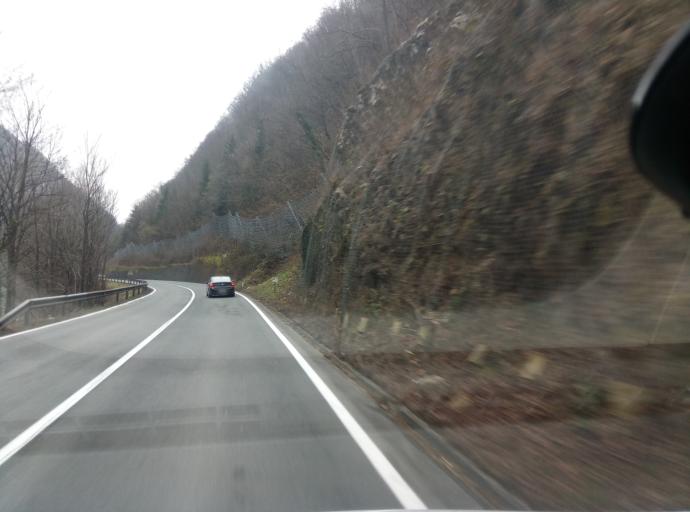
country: SI
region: Zagorje ob Savi
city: Kisovec
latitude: 46.1066
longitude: 14.9666
